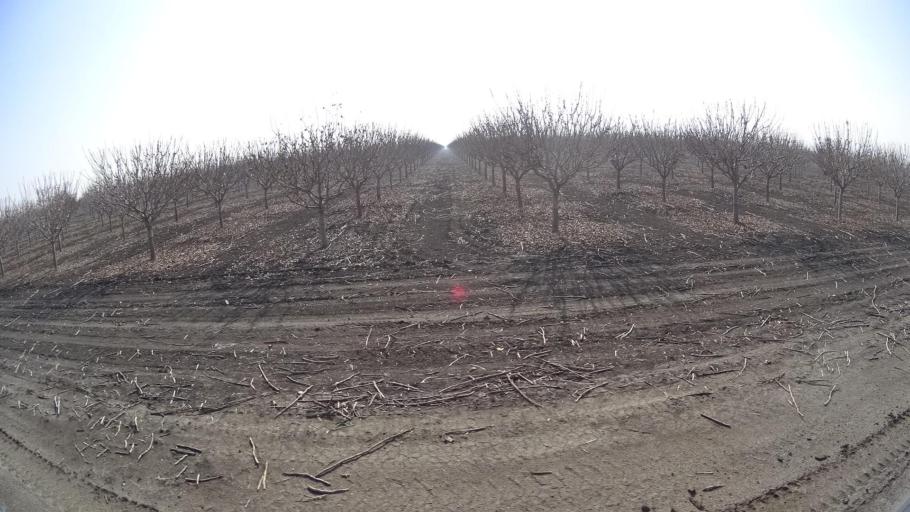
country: US
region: California
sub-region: Kern County
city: Buttonwillow
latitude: 35.3402
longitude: -119.4060
